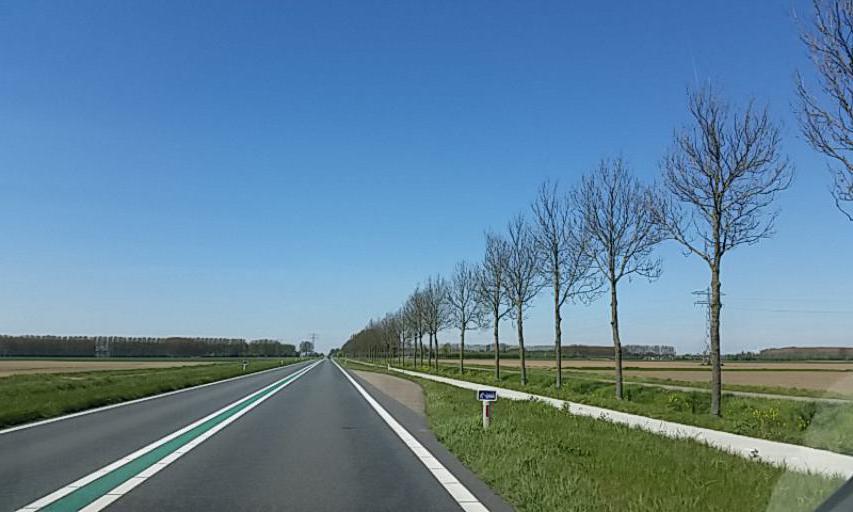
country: NL
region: Zeeland
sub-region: Gemeente Terneuzen
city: Koewacht
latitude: 51.2588
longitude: 3.9535
